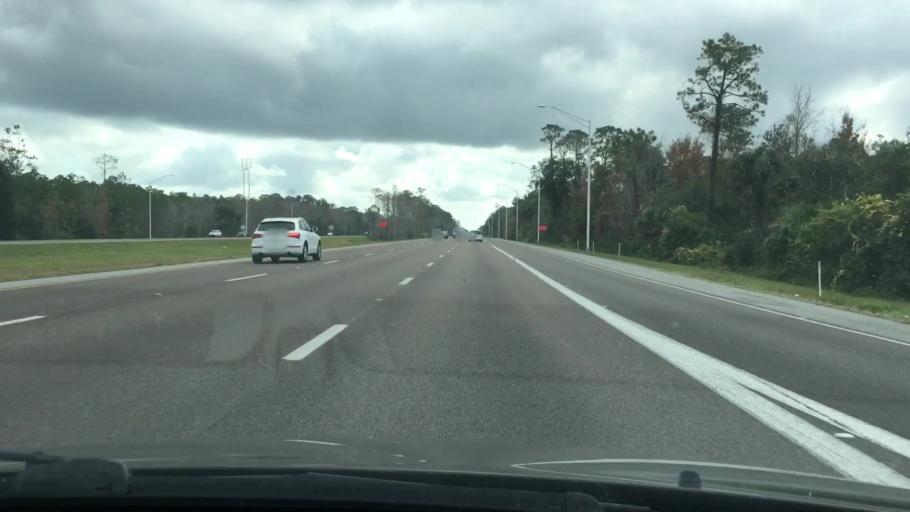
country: US
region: Florida
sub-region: Volusia County
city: Glencoe
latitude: 29.0095
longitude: -80.9861
